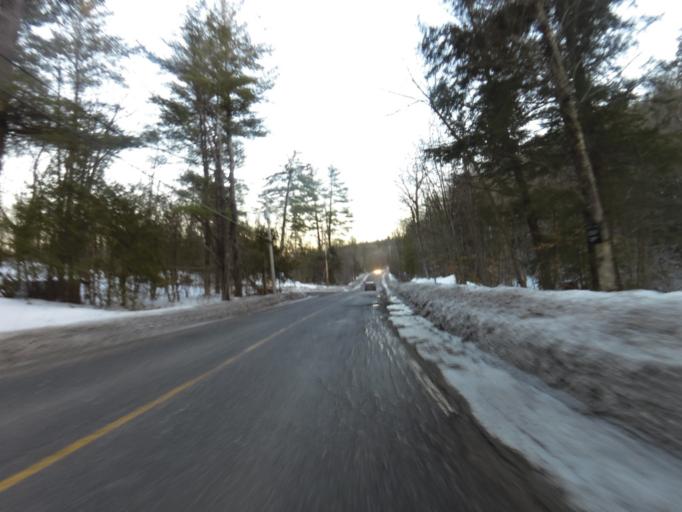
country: CA
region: Quebec
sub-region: Outaouais
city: Gatineau
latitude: 45.4845
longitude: -75.8076
